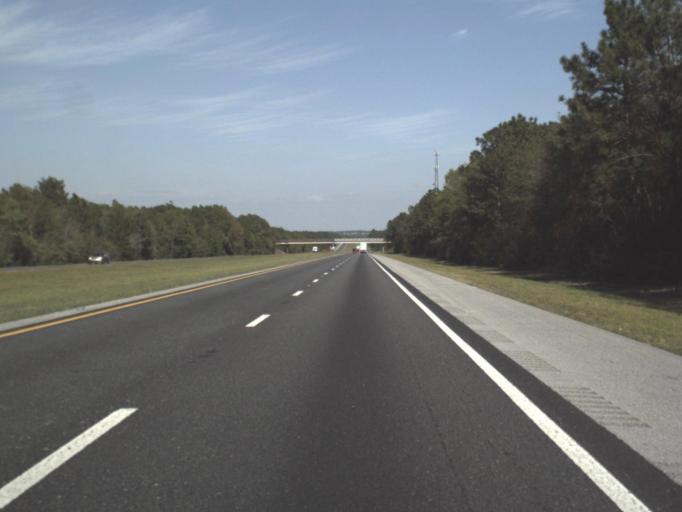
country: US
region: Florida
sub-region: Okaloosa County
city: Crestview
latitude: 30.7149
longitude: -86.6826
